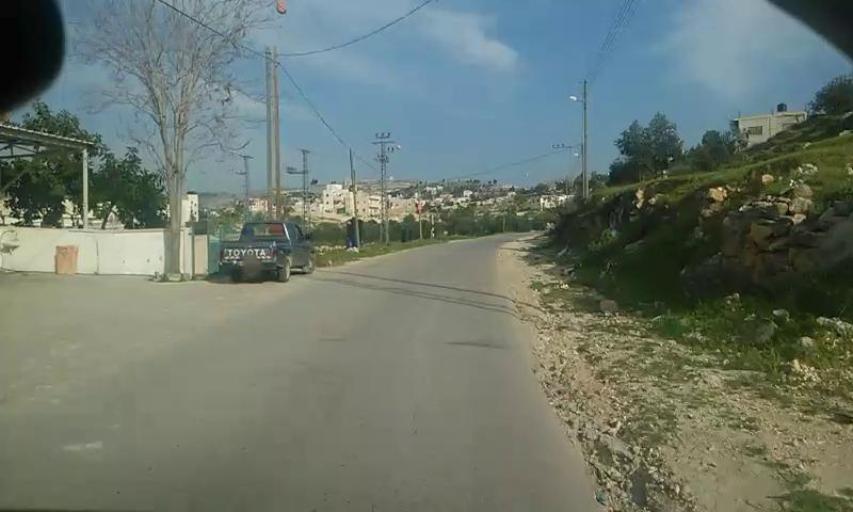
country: PS
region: West Bank
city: Nuba
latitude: 31.6137
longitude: 35.0327
